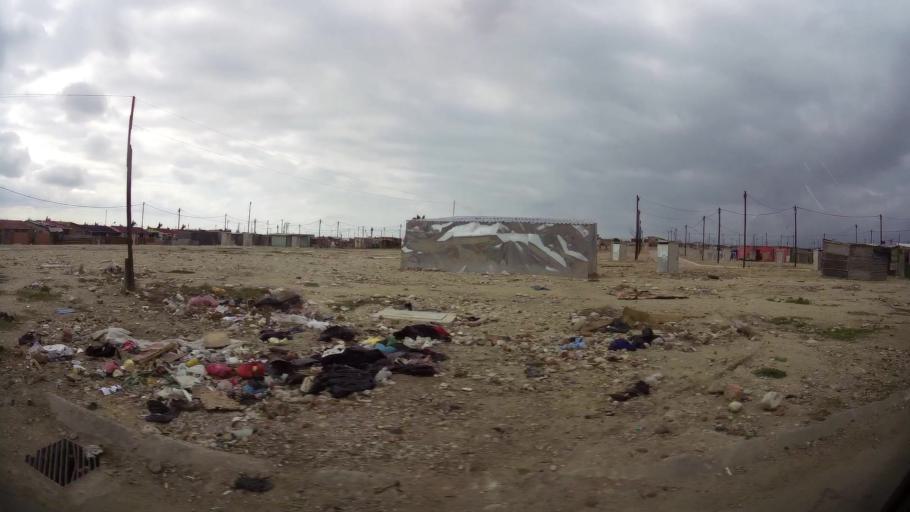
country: ZA
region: Eastern Cape
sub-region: Nelson Mandela Bay Metropolitan Municipality
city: Port Elizabeth
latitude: -33.8862
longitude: 25.6049
